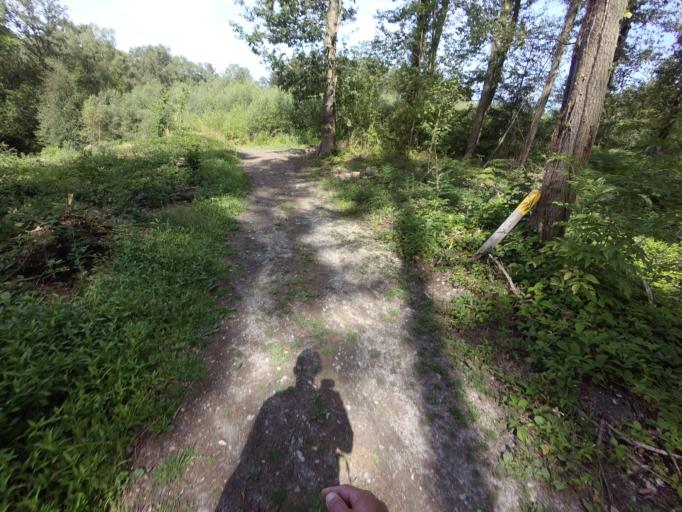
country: BE
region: Wallonia
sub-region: Province de Liege
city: Plombieres
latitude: 50.7690
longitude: 5.9420
